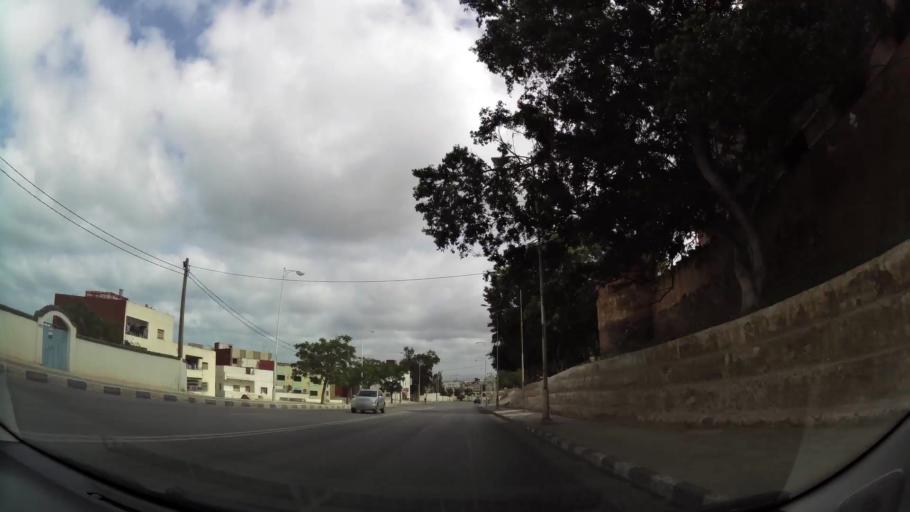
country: MA
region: Oriental
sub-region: Nador
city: Nador
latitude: 35.1876
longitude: -2.9291
